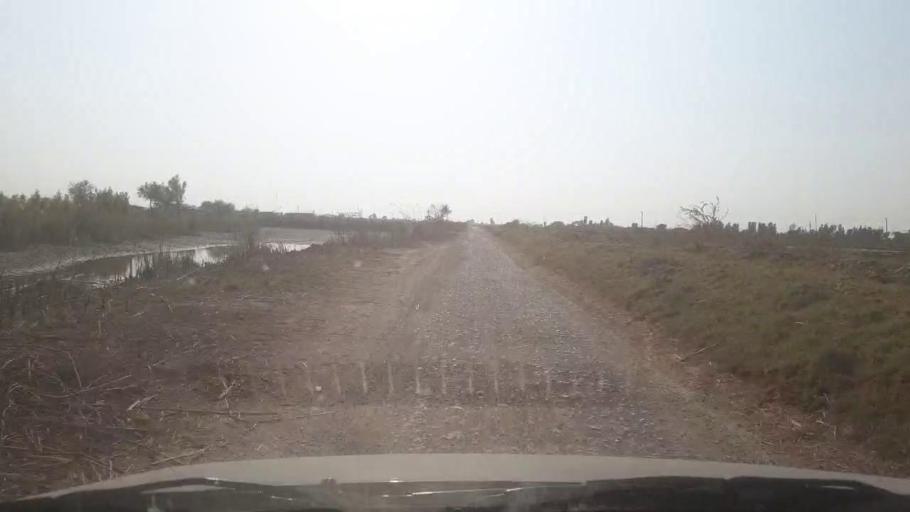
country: PK
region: Sindh
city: Samaro
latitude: 25.1536
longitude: 69.3851
